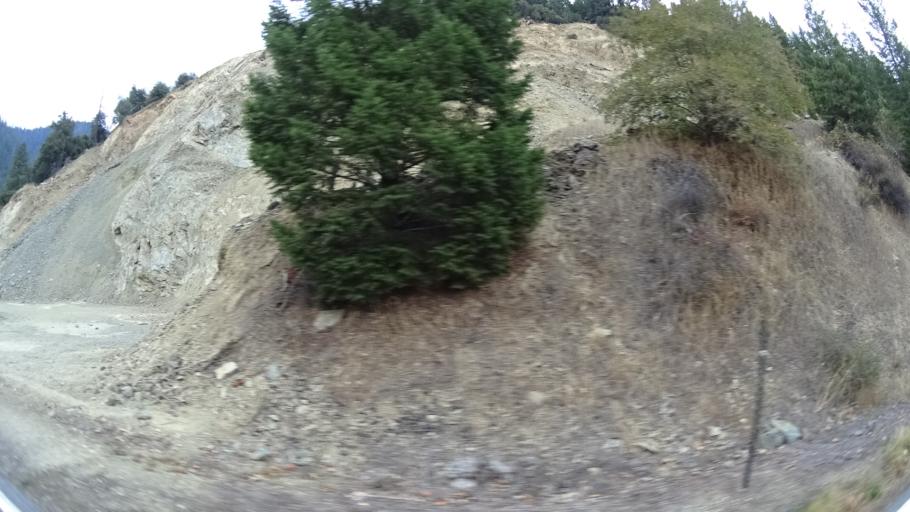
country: US
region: California
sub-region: Siskiyou County
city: Happy Camp
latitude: 41.8828
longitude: -123.4288
